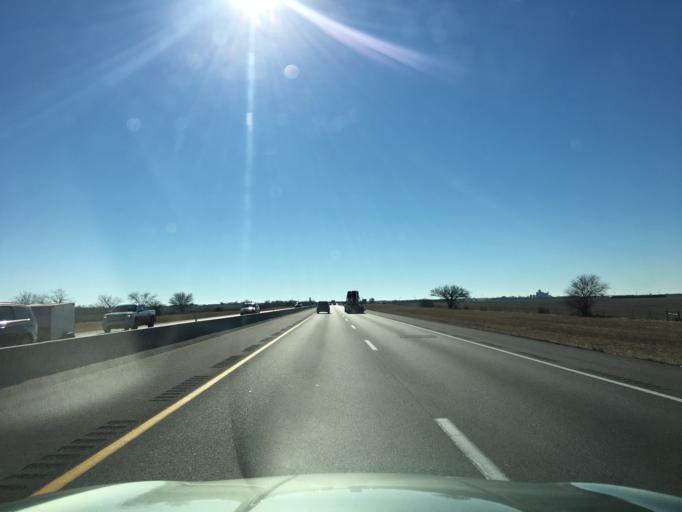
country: US
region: Kansas
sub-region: Sumner County
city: Wellington
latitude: 37.2982
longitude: -97.3404
